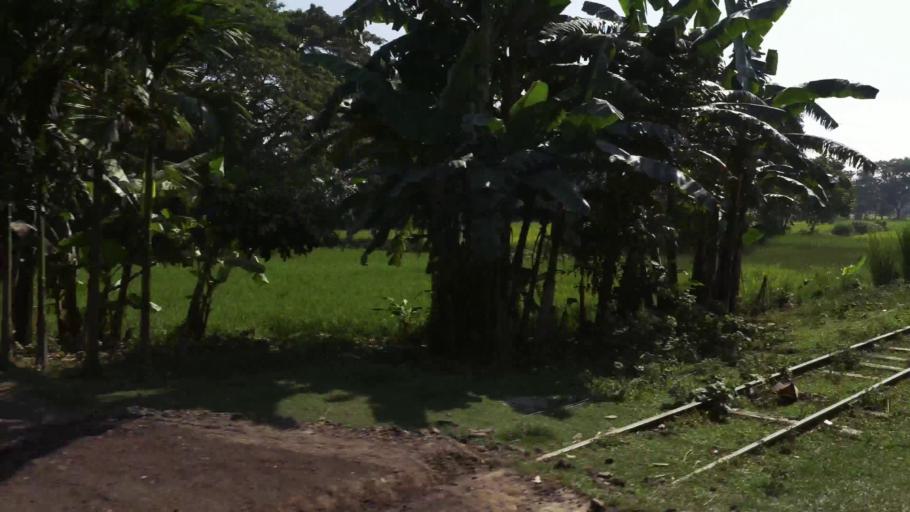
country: BD
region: Dhaka
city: Gafargaon
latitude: 24.5897
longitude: 90.5050
